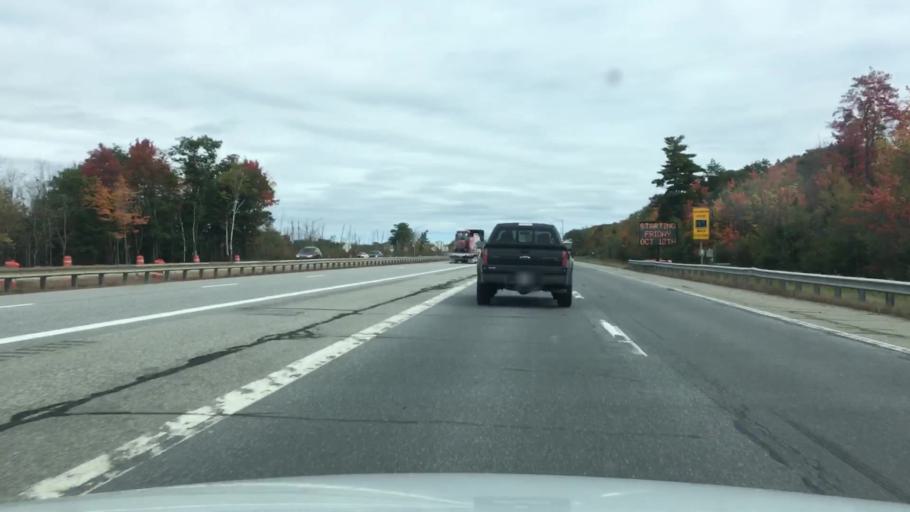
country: US
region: Maine
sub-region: Kennebec County
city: Gardiner
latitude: 44.2214
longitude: -69.8203
